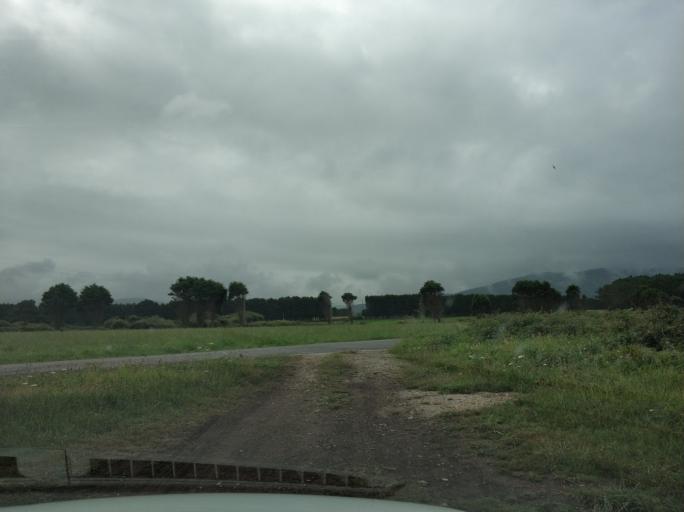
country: ES
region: Asturias
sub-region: Province of Asturias
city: Tineo
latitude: 43.5682
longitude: -6.4702
